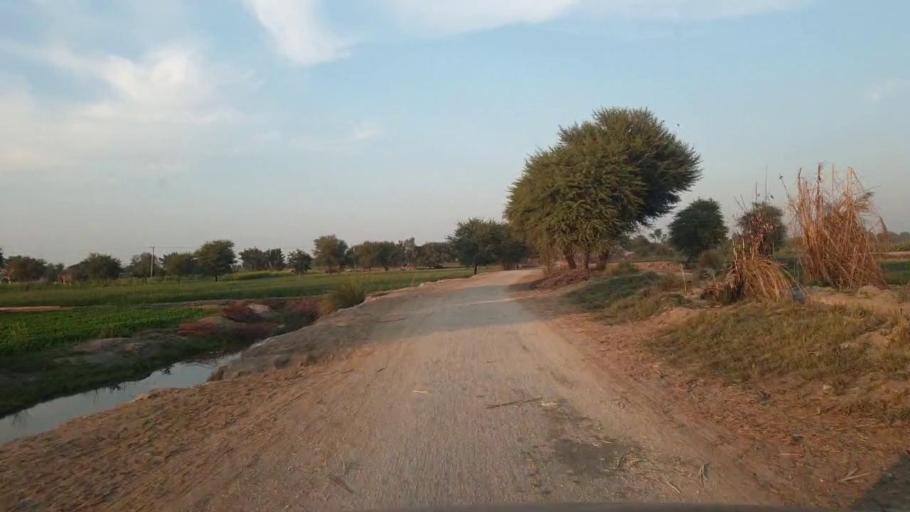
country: PK
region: Sindh
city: Shahpur Chakar
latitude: 26.1971
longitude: 68.6187
